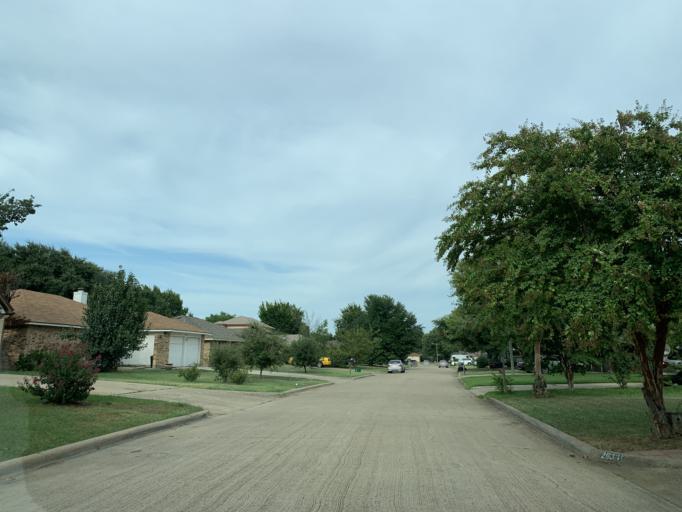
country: US
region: Texas
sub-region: Dallas County
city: Grand Prairie
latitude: 32.6633
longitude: -97.0448
